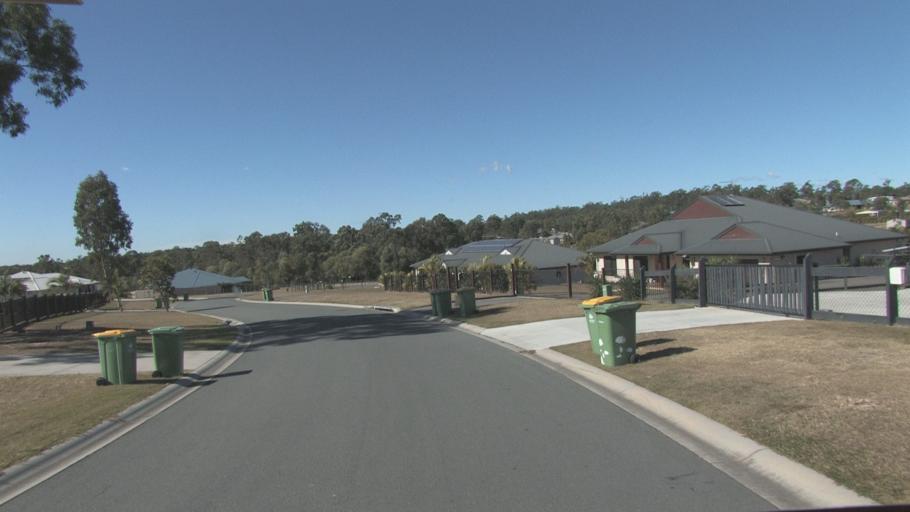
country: AU
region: Queensland
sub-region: Logan
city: North Maclean
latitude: -27.7565
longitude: 152.9470
